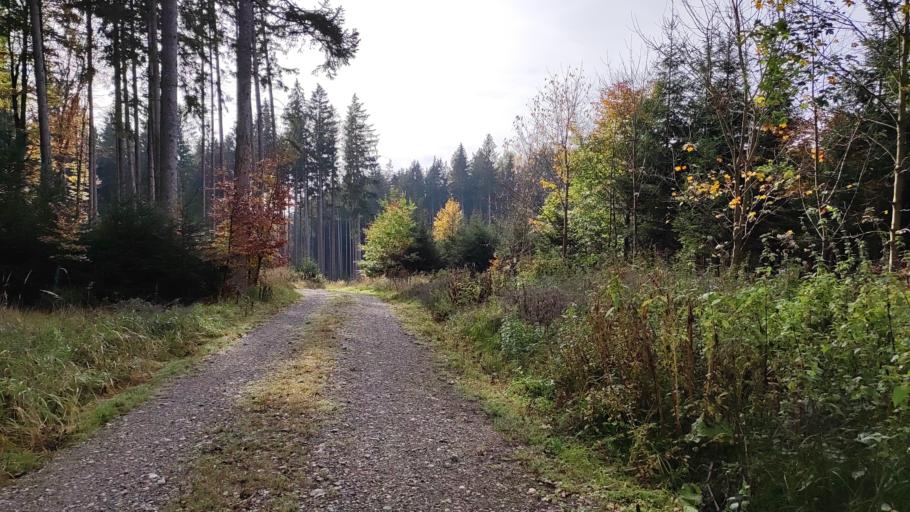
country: DE
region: Bavaria
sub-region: Swabia
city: Langenneufnach
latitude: 48.2947
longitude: 10.5866
